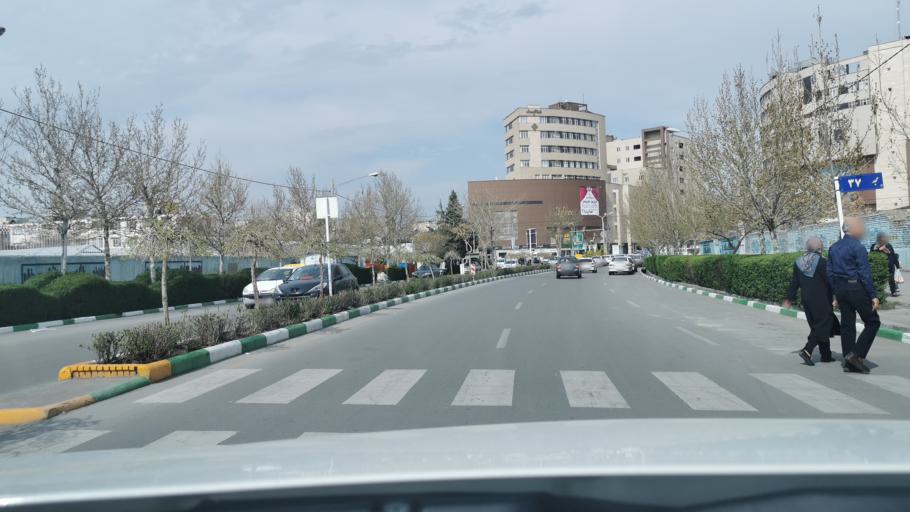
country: IR
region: Razavi Khorasan
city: Mashhad
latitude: 36.3114
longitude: 59.5894
